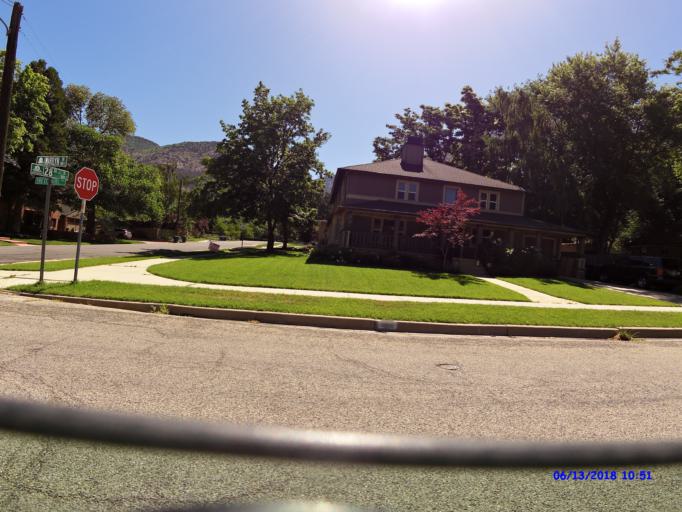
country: US
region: Utah
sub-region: Weber County
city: Ogden
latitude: 41.2139
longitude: -111.9404
